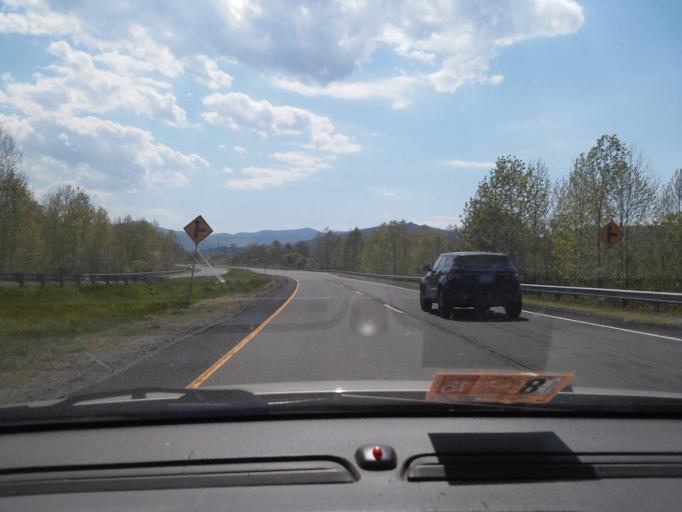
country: US
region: Virginia
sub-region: Rappahannock County
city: Washington
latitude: 38.6846
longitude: -78.2013
